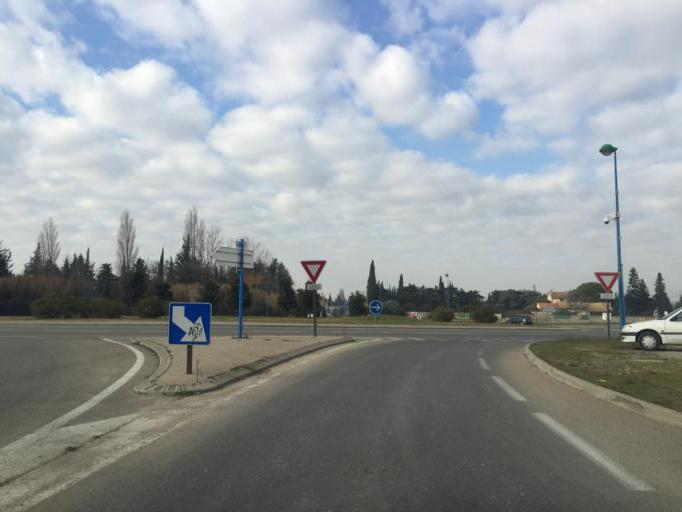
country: FR
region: Provence-Alpes-Cote d'Azur
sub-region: Departement du Vaucluse
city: Carpentras
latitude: 44.0604
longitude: 5.0393
